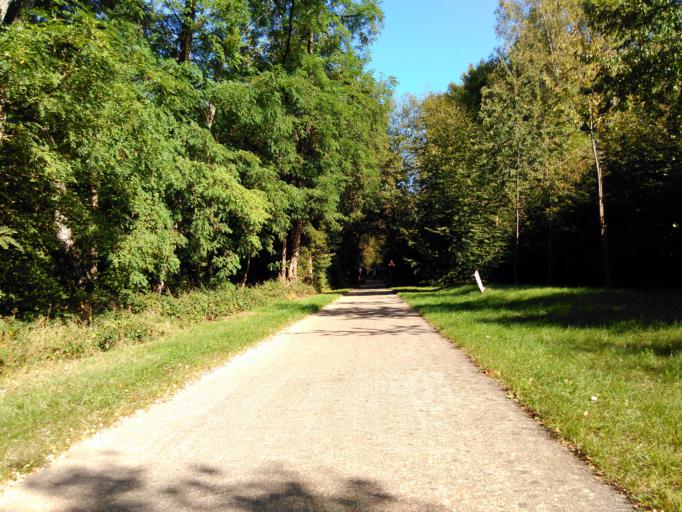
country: LU
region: Luxembourg
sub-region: Canton de Capellen
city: Hobscheid
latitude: 49.6965
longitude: 5.9033
